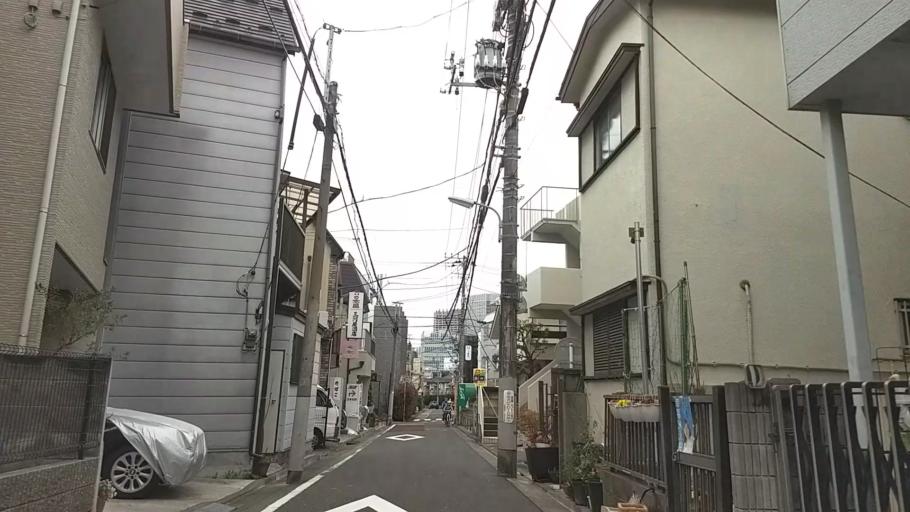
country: JP
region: Tokyo
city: Tokyo
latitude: 35.6185
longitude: 139.7215
